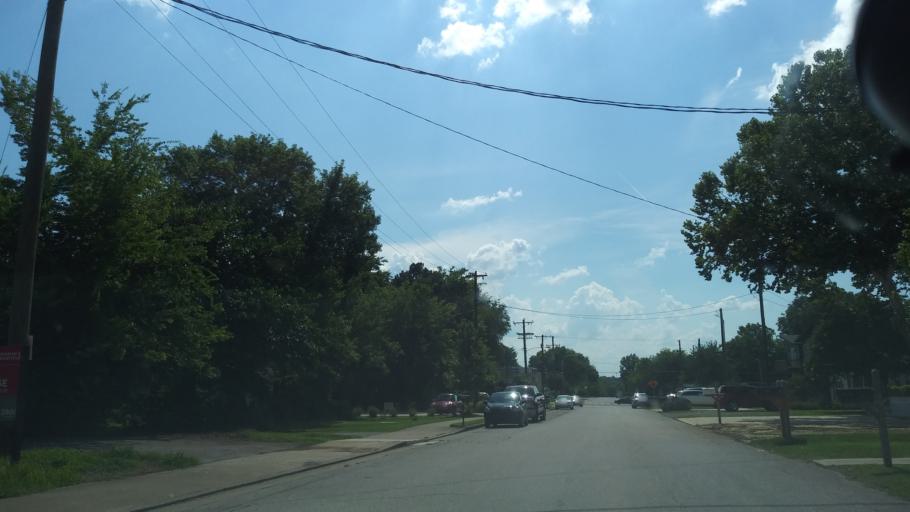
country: US
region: Tennessee
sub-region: Davidson County
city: Belle Meade
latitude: 36.1566
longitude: -86.8472
